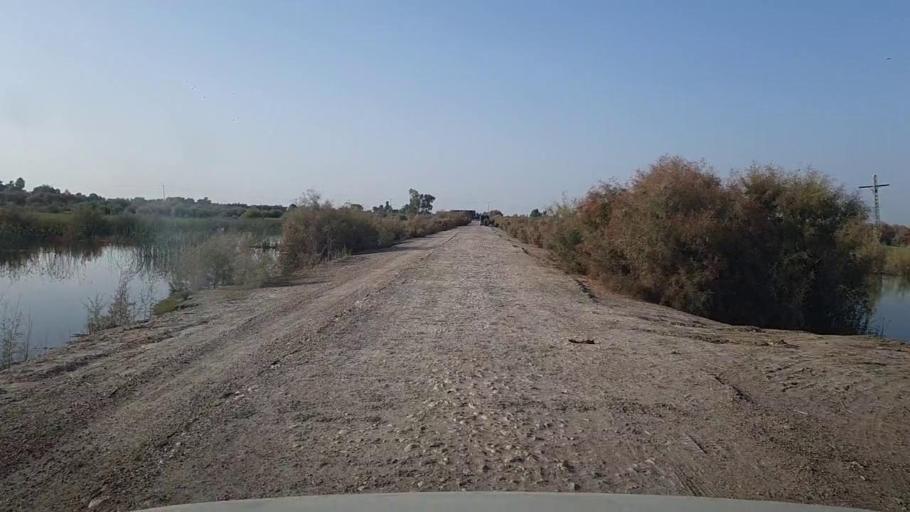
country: PK
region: Sindh
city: Kandhkot
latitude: 28.3087
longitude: 69.3280
